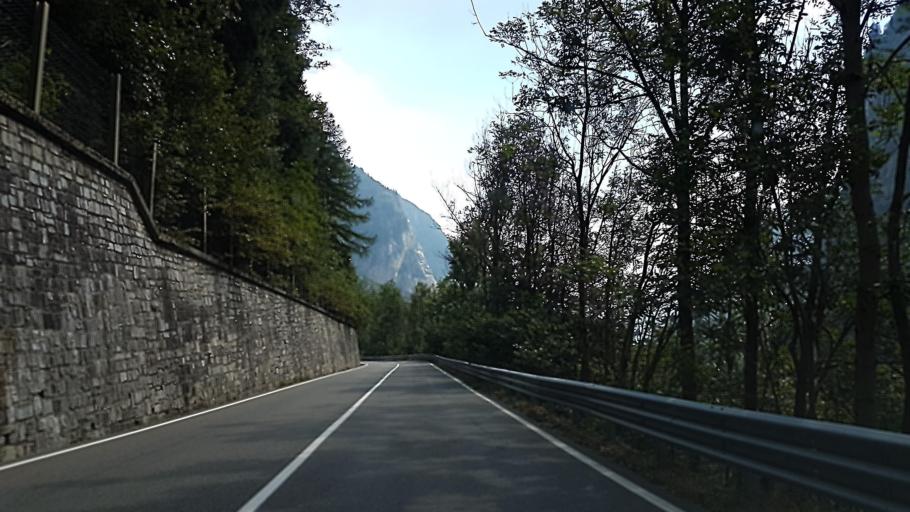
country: IT
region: Lombardy
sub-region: Provincia di Sondrio
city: Campodolcino
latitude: 46.3789
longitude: 9.3560
